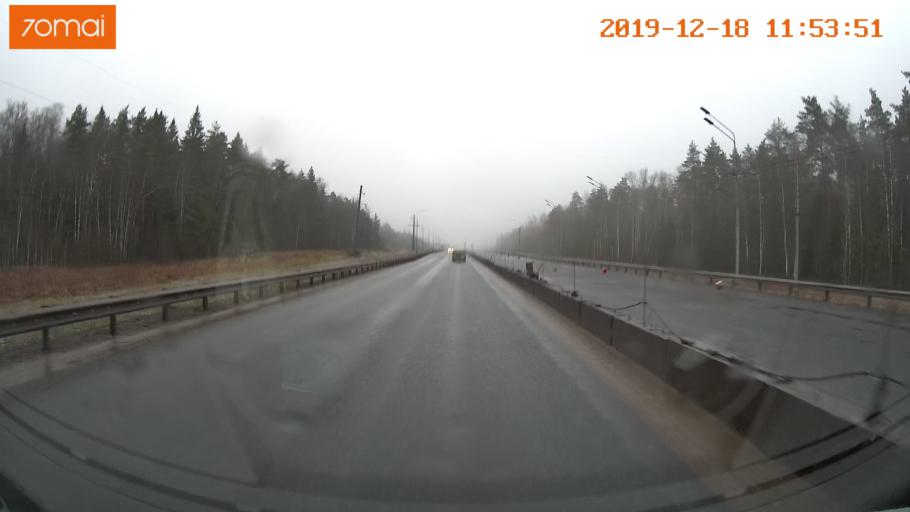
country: RU
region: Moskovskaya
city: Yershovo
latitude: 55.8091
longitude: 36.9192
